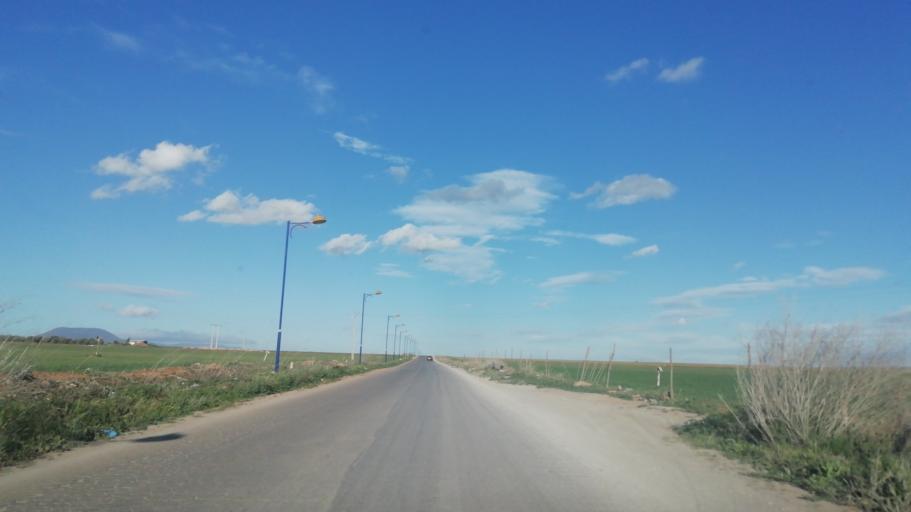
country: DZ
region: Oran
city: Sidi ech Chahmi
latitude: 35.6423
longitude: -0.5378
